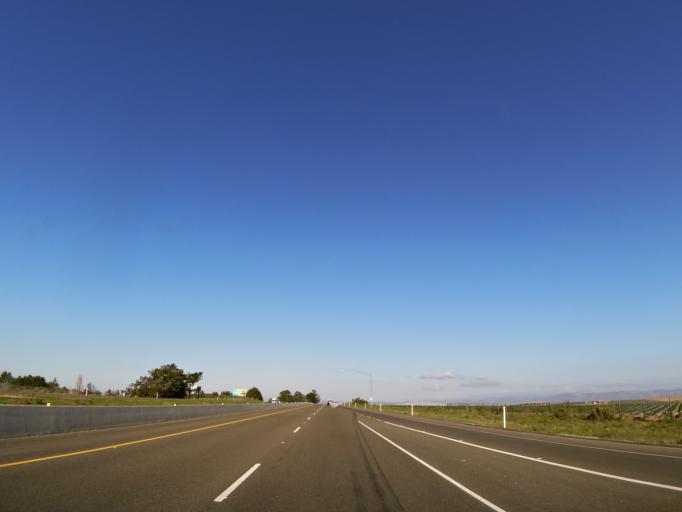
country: US
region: California
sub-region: Santa Barbara County
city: Orcutt
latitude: 34.8674
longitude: -120.3977
